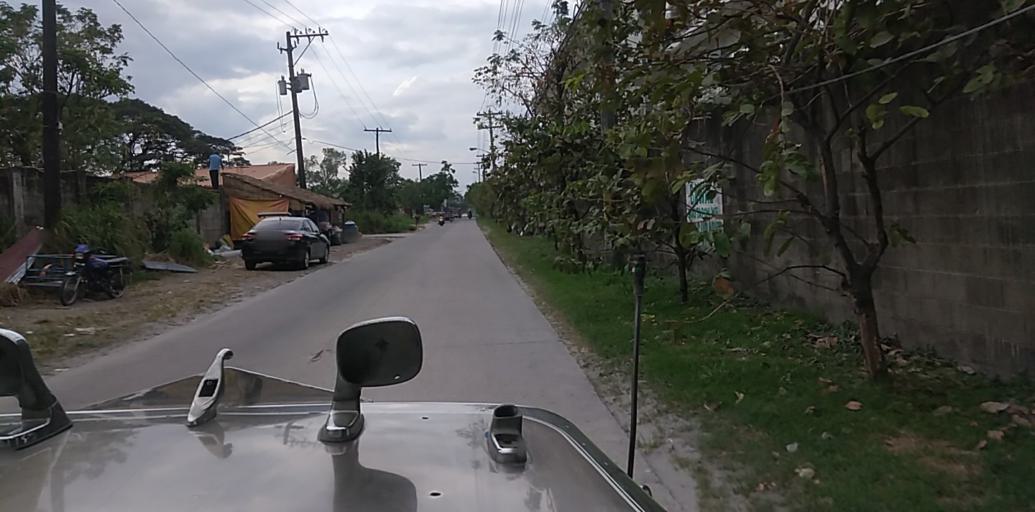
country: PH
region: Central Luzon
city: Santol
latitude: 15.1649
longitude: 120.5467
